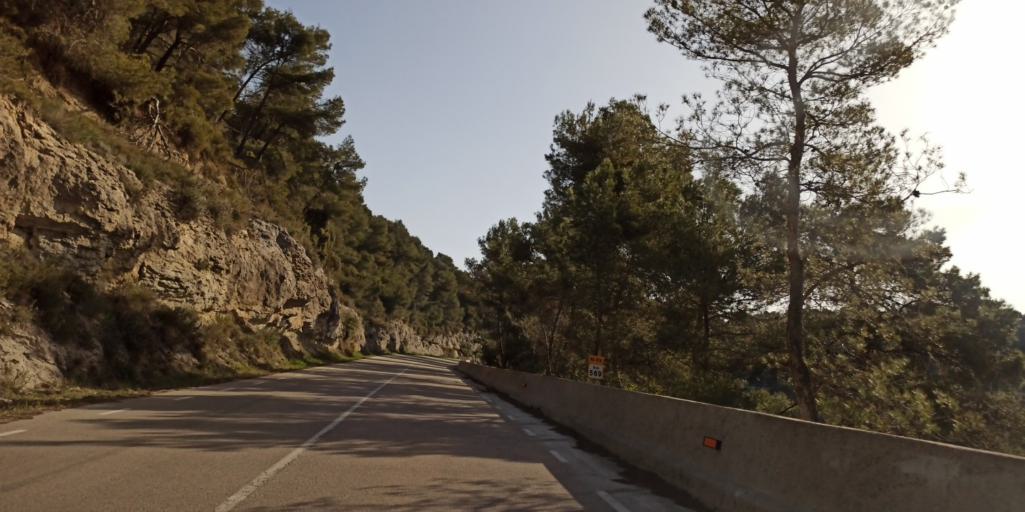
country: ES
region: Catalonia
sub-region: Provincia de Barcelona
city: Castelloli
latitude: 41.5968
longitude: 1.7278
